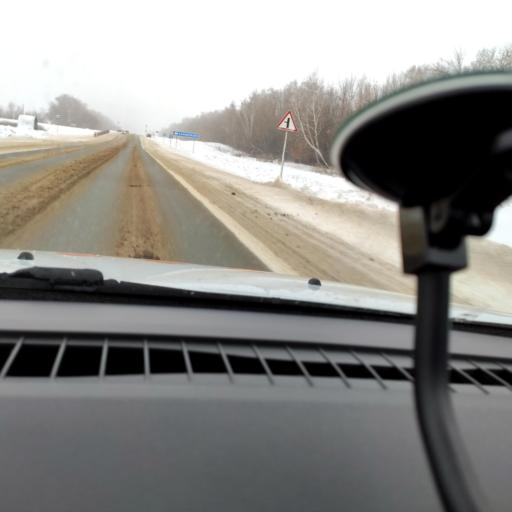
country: RU
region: Samara
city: Dubovyy Umet
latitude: 53.0327
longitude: 50.2169
